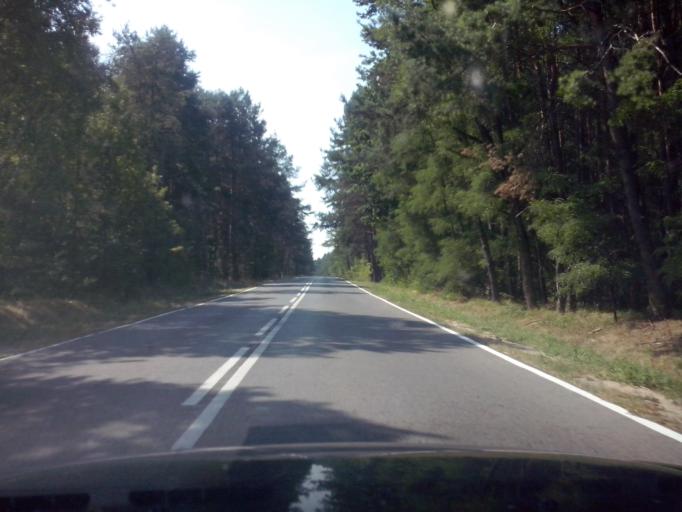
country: PL
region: Swietokrzyskie
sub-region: Powiat staszowski
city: Szydlow
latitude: 50.6244
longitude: 21.0204
